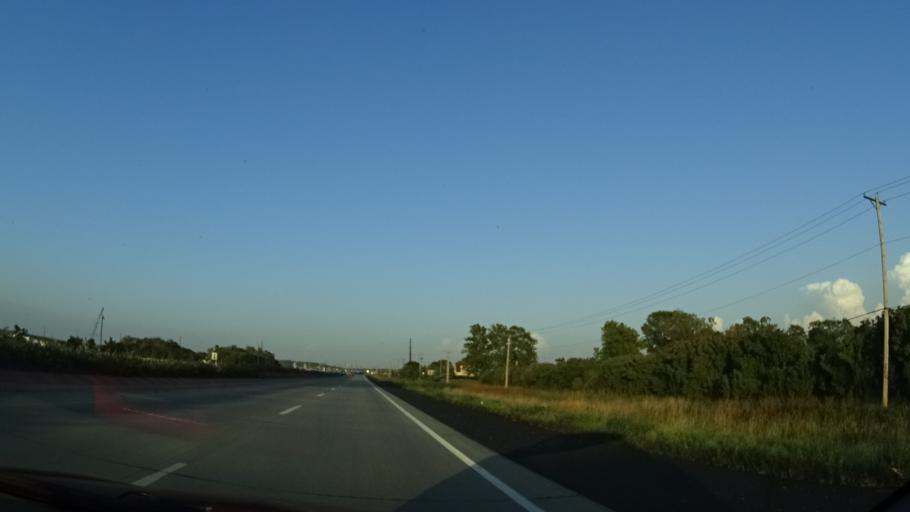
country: US
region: Iowa
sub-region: Pottawattamie County
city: Council Bluffs
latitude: 41.2170
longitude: -95.8833
